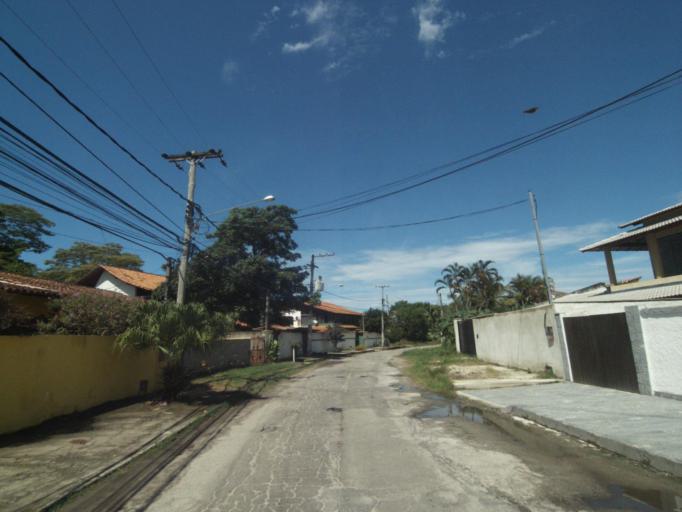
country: BR
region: Rio de Janeiro
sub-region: Niteroi
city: Niteroi
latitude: -22.9454
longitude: -43.0405
